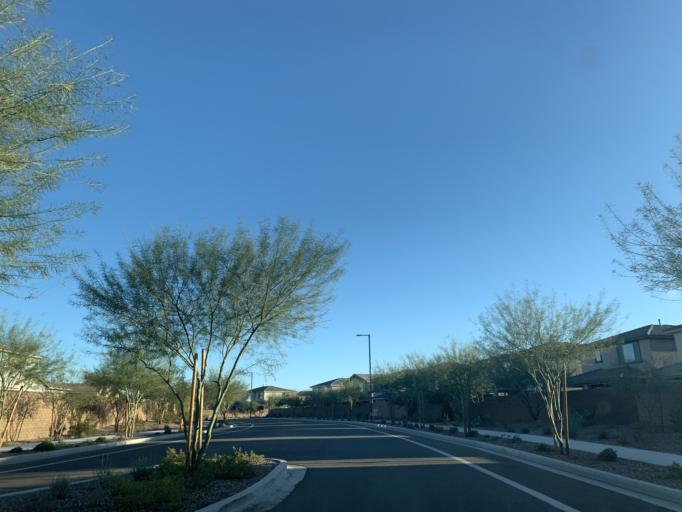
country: US
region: Arizona
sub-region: Maricopa County
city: Cave Creek
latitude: 33.6880
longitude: -112.0193
